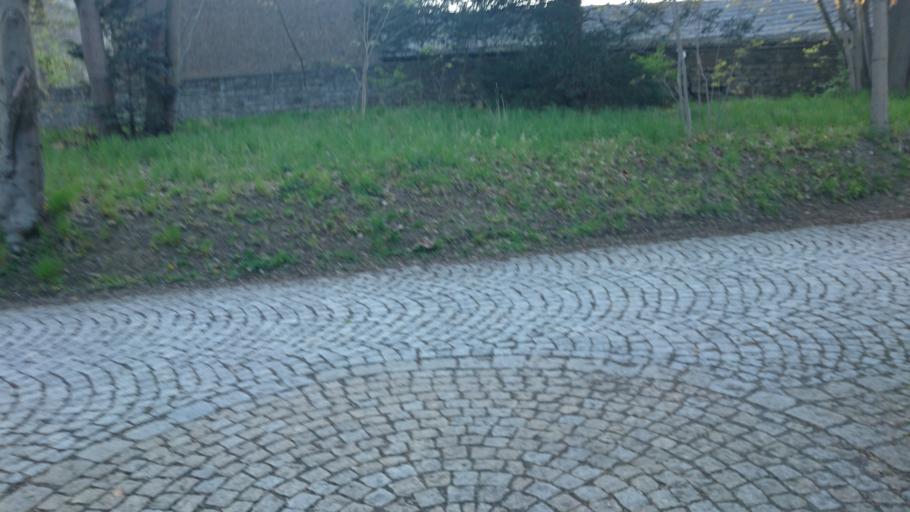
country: DE
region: Thuringia
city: Schleiz
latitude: 50.5762
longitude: 11.8127
